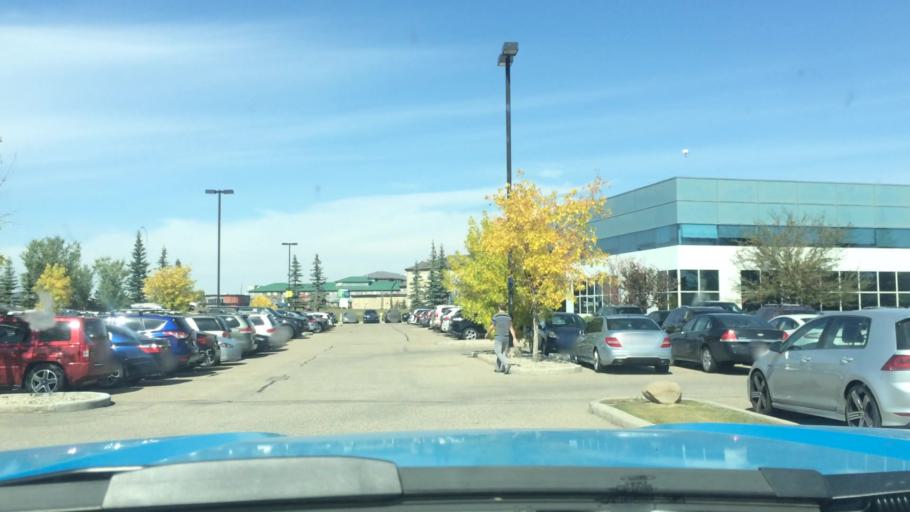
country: CA
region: Alberta
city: Calgary
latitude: 51.0915
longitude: -113.9978
